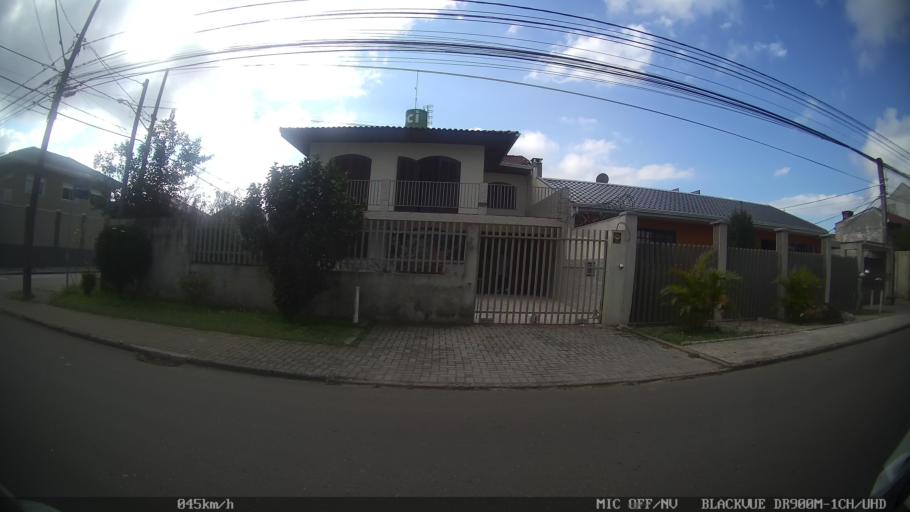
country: BR
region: Parana
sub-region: Pinhais
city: Pinhais
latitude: -25.4029
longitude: -49.1881
